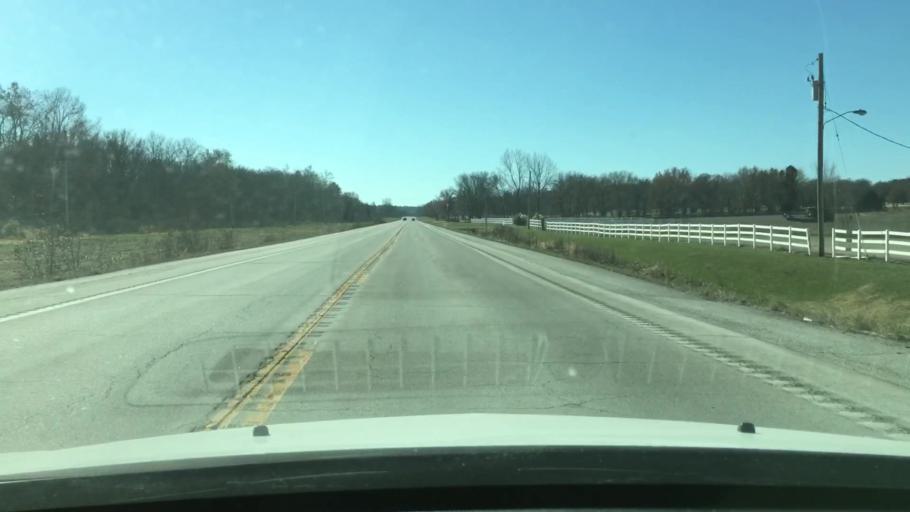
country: US
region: Missouri
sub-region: Pike County
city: Louisiana
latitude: 39.4088
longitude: -91.1040
